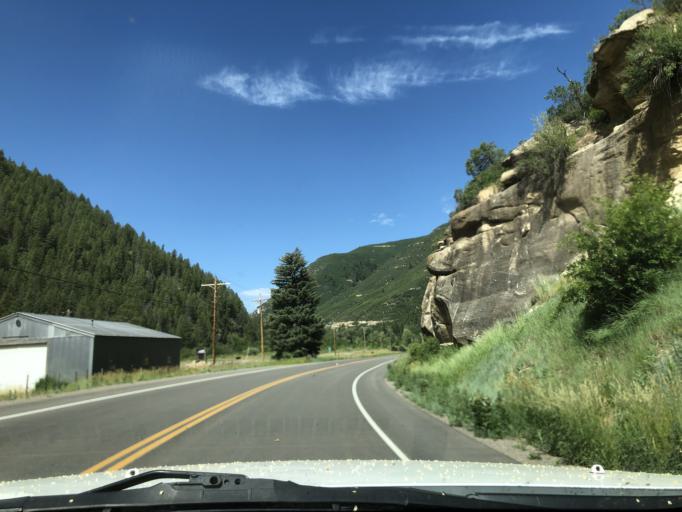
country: US
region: Colorado
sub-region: Delta County
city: Paonia
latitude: 38.9380
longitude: -107.3749
